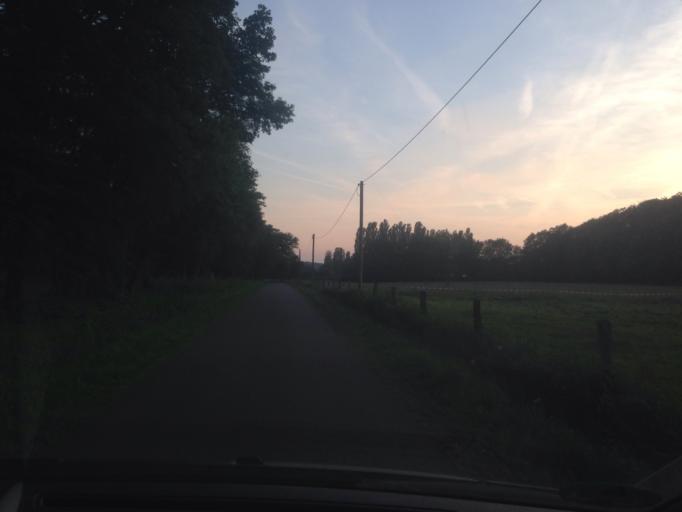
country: DE
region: North Rhine-Westphalia
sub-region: Regierungsbezirk Munster
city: Greven
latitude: 52.0231
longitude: 7.5706
